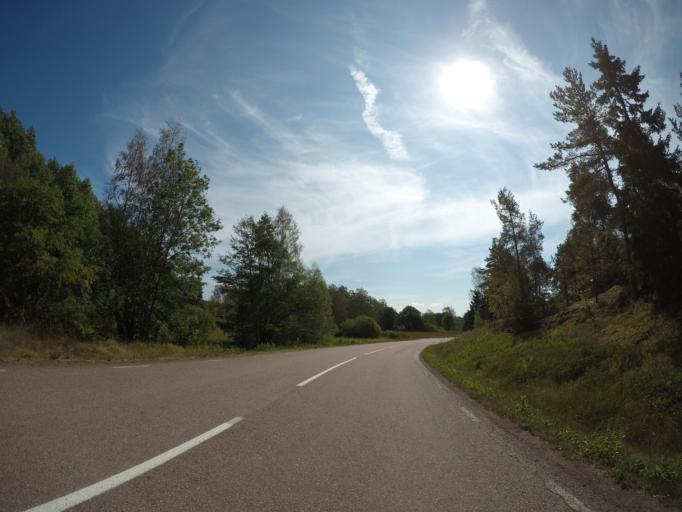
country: AX
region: Alands landsbygd
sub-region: Finstroem
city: Finstroem
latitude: 60.2745
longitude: 19.9188
